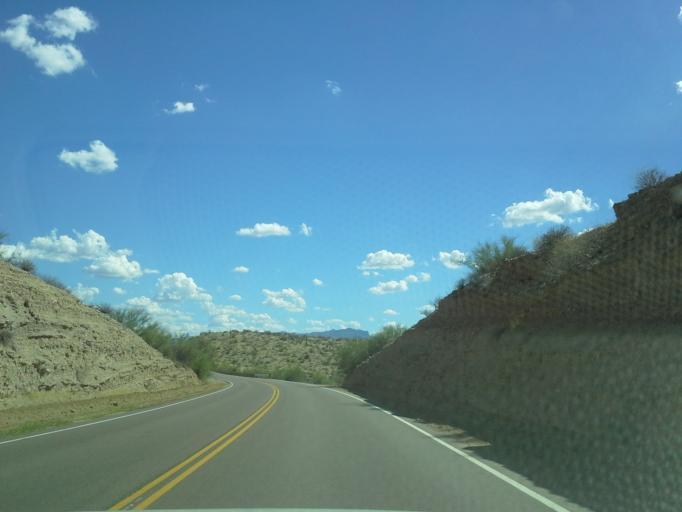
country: US
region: Arizona
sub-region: Maricopa County
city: Fountain Hills
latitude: 33.6130
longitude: -111.5531
